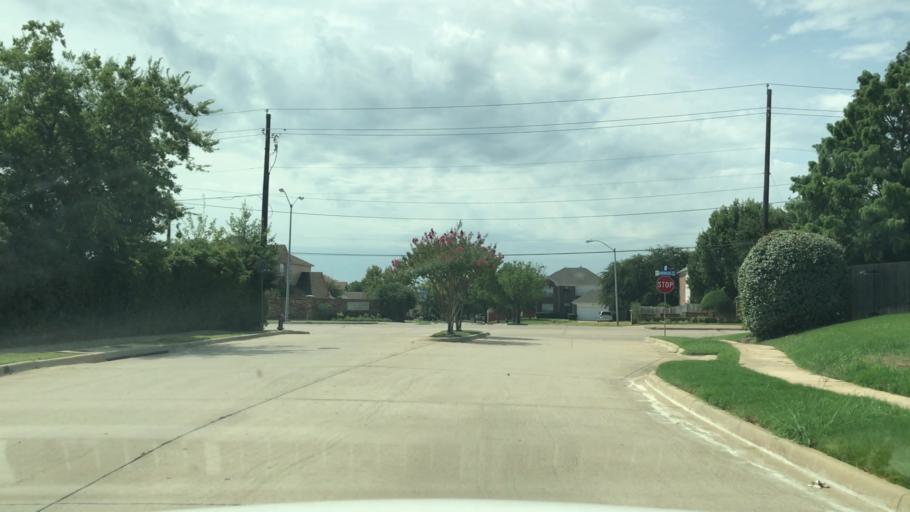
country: US
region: Texas
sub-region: Tarrant County
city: Euless
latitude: 32.8522
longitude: -97.0773
